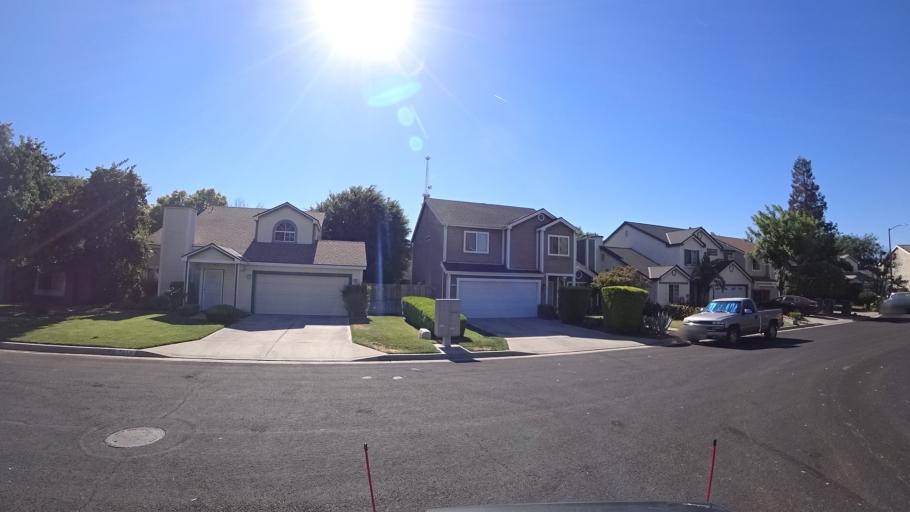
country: US
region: California
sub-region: Fresno County
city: West Park
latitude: 36.7848
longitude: -119.8558
